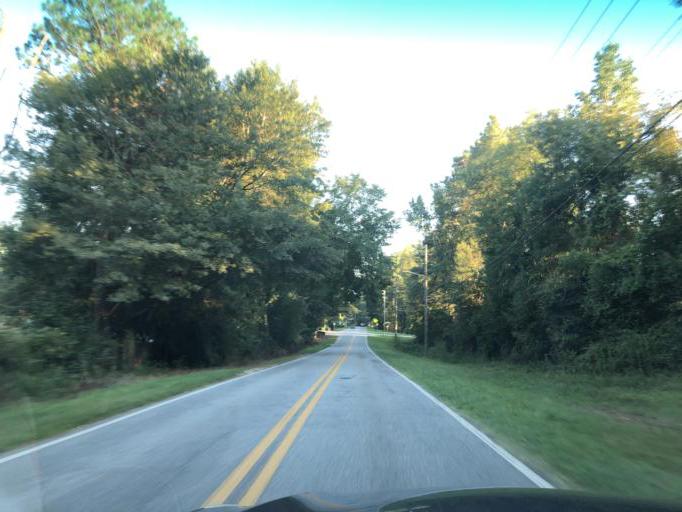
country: US
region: Georgia
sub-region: Muscogee County
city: Columbus
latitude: 32.5362
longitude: -84.8927
